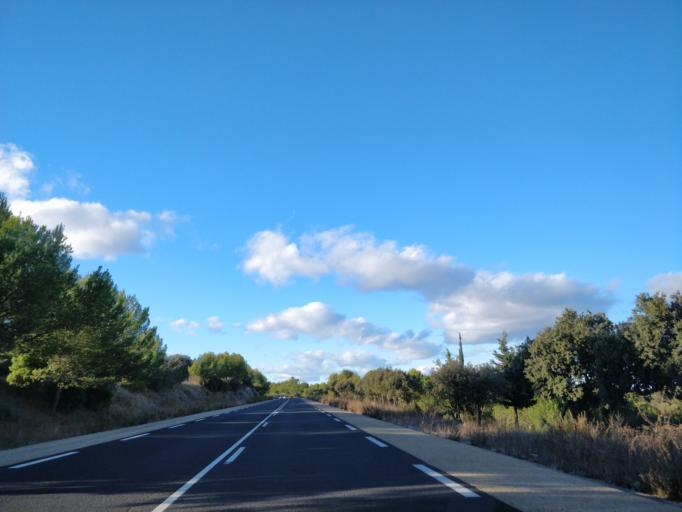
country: FR
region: Languedoc-Roussillon
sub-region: Departement de l'Herault
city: Vendargues
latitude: 43.6717
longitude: 3.9588
